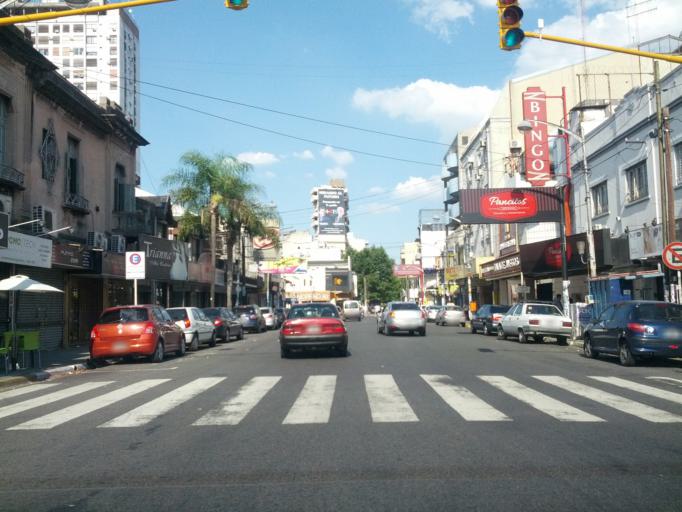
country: AR
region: Buenos Aires
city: San Justo
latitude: -34.6416
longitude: -58.5641
